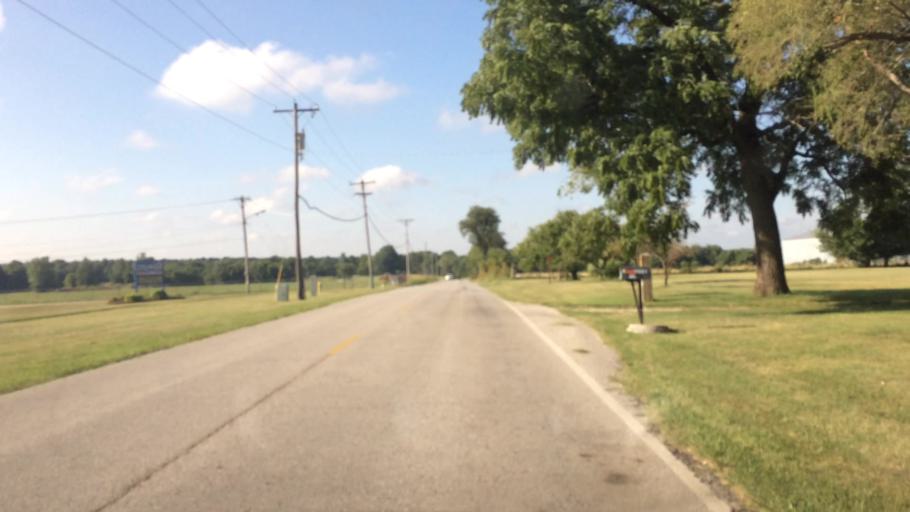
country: US
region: Missouri
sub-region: Greene County
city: Springfield
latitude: 37.2671
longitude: -93.2816
